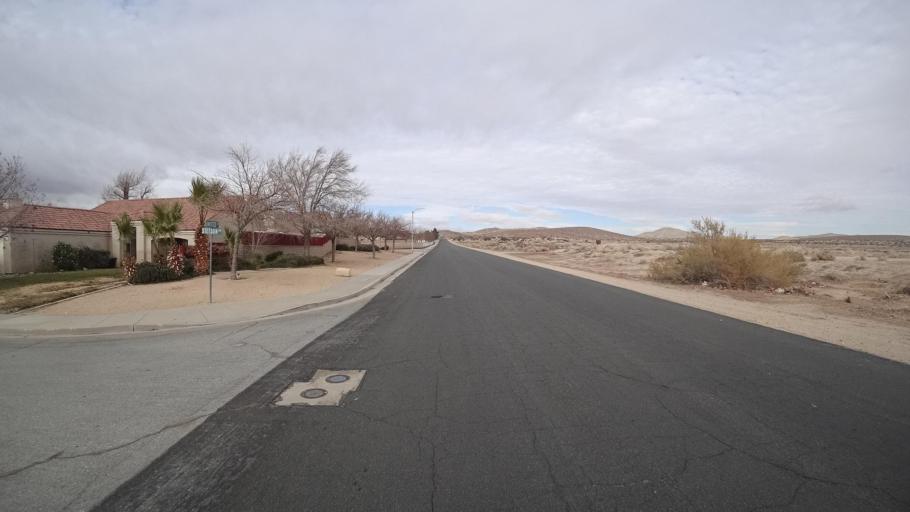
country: US
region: California
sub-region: Kern County
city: Rosamond
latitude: 34.8683
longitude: -118.1495
